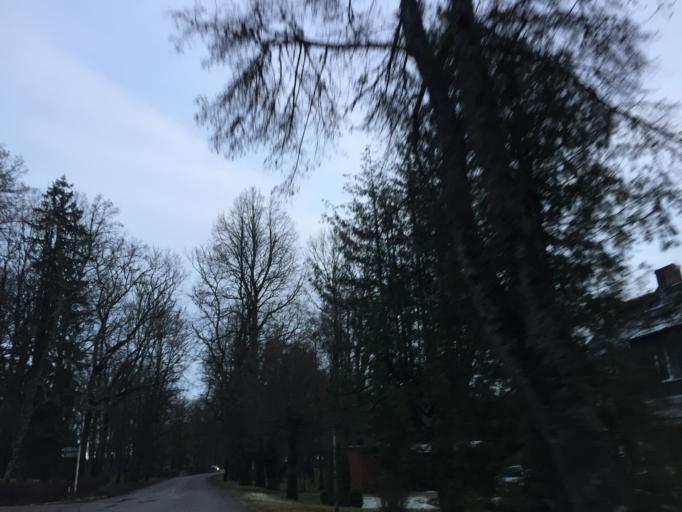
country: LV
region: Burtnieki
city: Matisi
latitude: 57.6374
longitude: 25.0447
